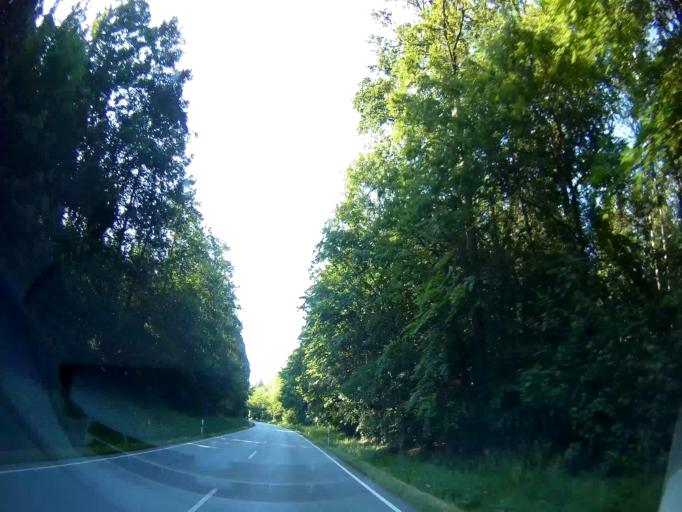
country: DE
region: Bavaria
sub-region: Lower Bavaria
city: Eggenfelden
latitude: 48.4119
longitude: 12.7774
